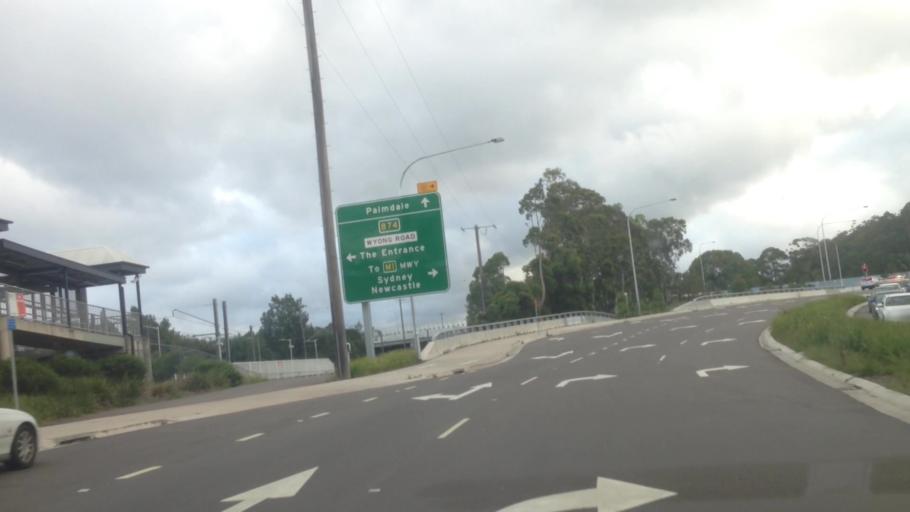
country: AU
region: New South Wales
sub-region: Wyong Shire
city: Chittaway Bay
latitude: -33.3077
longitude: 151.4198
